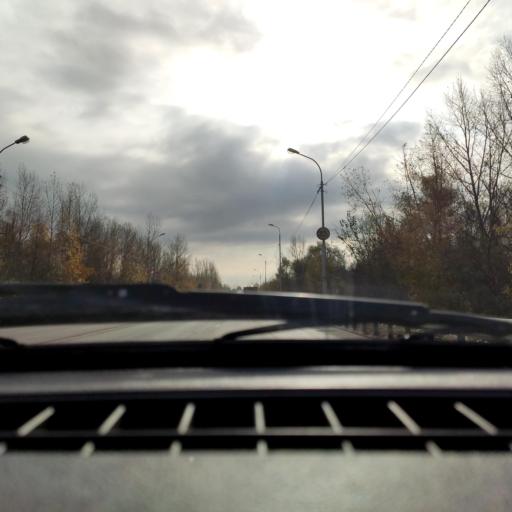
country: RU
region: Bashkortostan
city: Iglino
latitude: 54.7937
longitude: 56.2097
